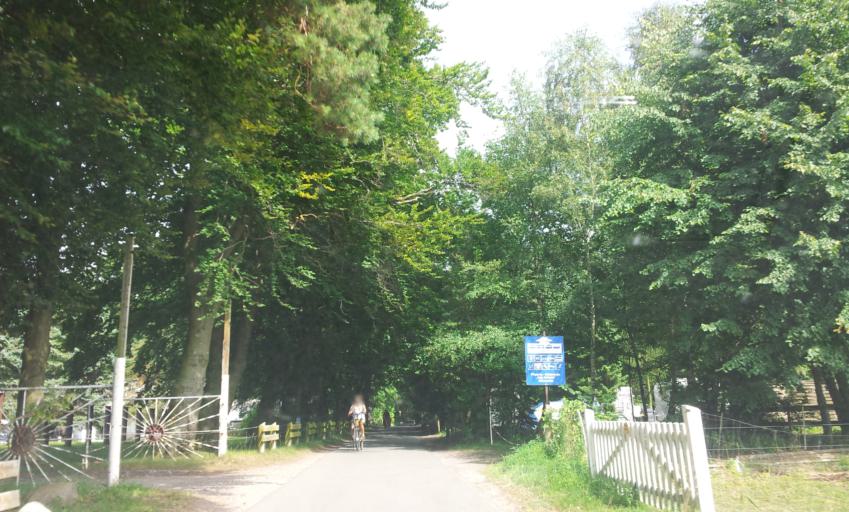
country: DE
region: Mecklenburg-Vorpommern
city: Wiek
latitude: 54.6679
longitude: 13.3025
